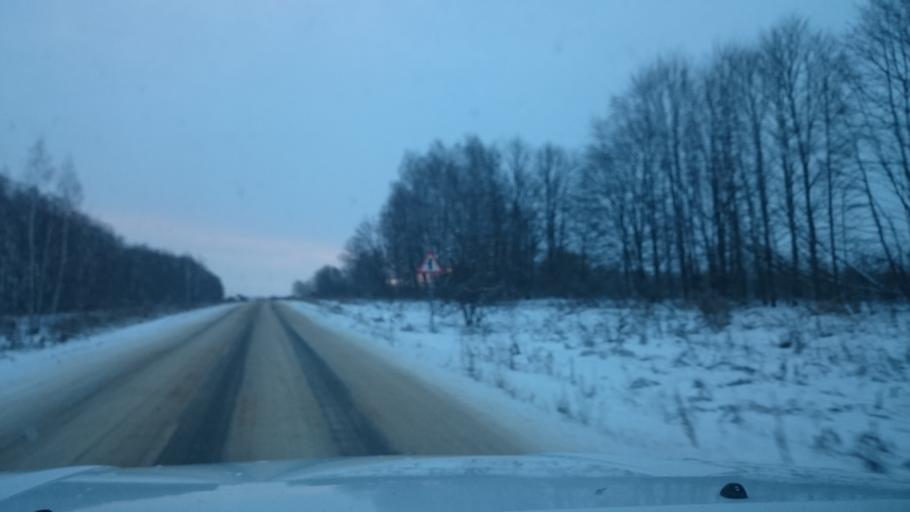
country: RU
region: Tula
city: Leninskiy
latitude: 54.2430
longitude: 37.2784
